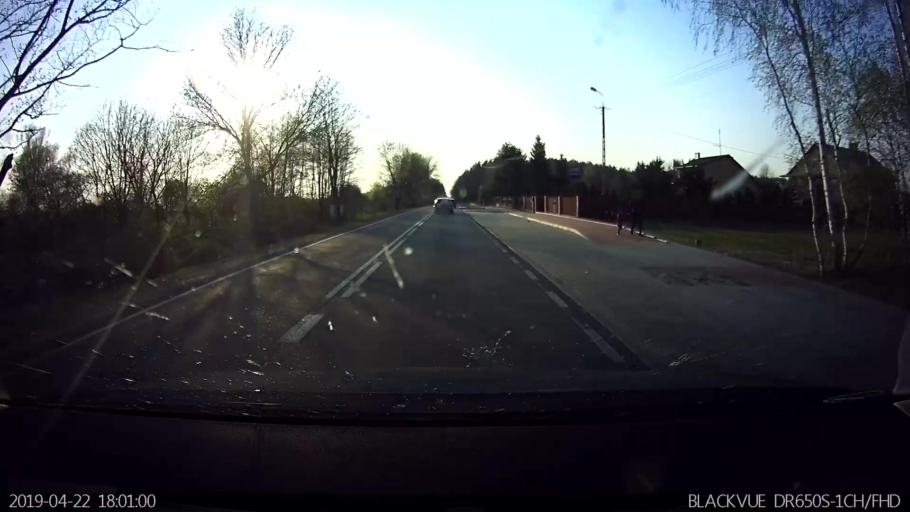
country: PL
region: Masovian Voivodeship
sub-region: Powiat wegrowski
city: Korytnica
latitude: 52.4770
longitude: 21.8374
